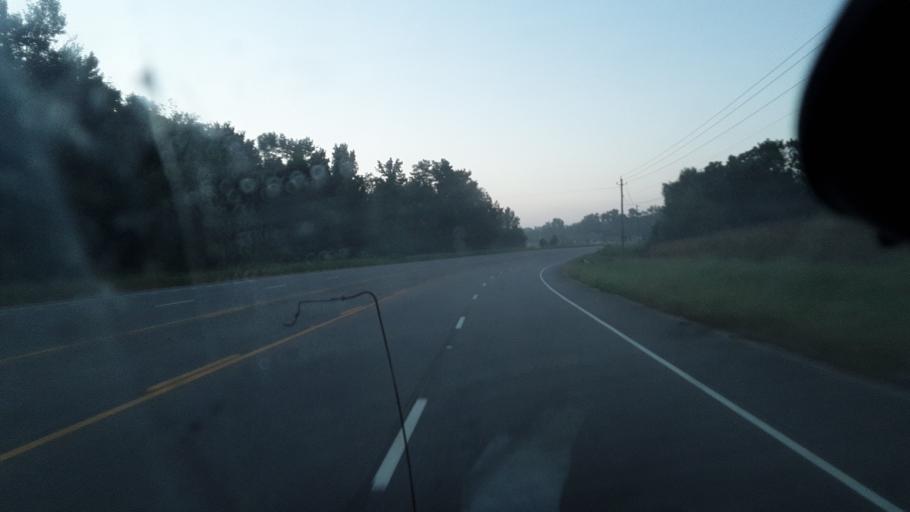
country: US
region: South Carolina
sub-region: Sumter County
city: Lakewood
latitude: 33.8665
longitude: -80.3169
